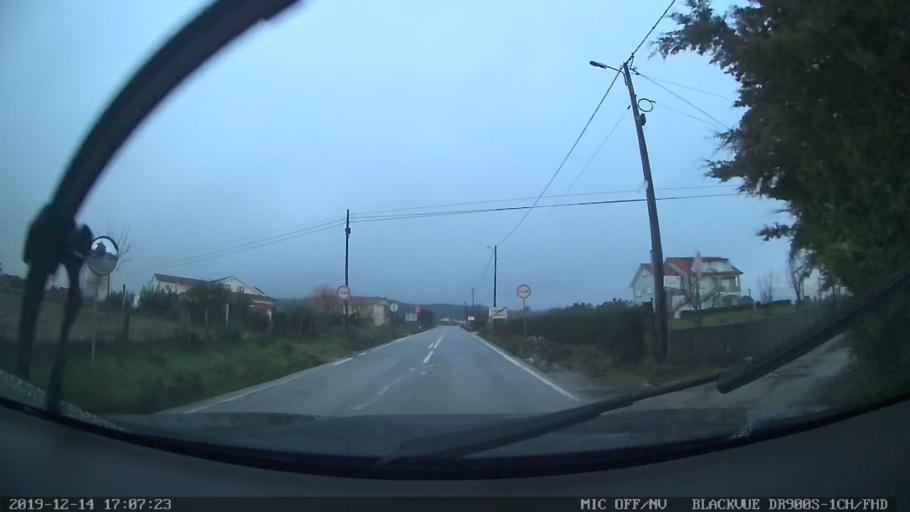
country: PT
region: Vila Real
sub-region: Vila Pouca de Aguiar
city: Vila Pouca de Aguiar
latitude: 41.4613
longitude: -7.5978
